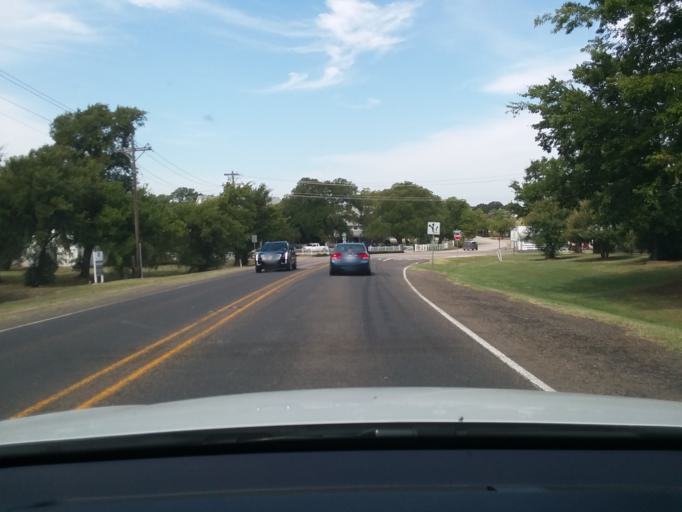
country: US
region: Texas
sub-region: Denton County
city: Bartonville
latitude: 33.0738
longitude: -97.1306
